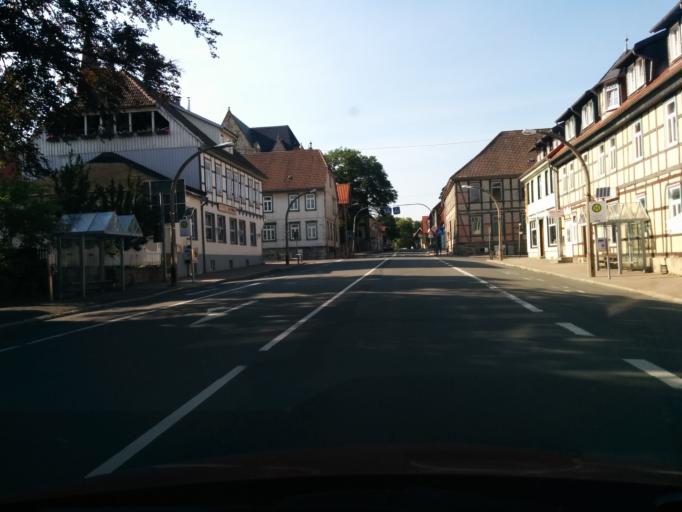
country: DE
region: Saxony-Anhalt
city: Elbingerode
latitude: 51.7701
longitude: 10.8034
